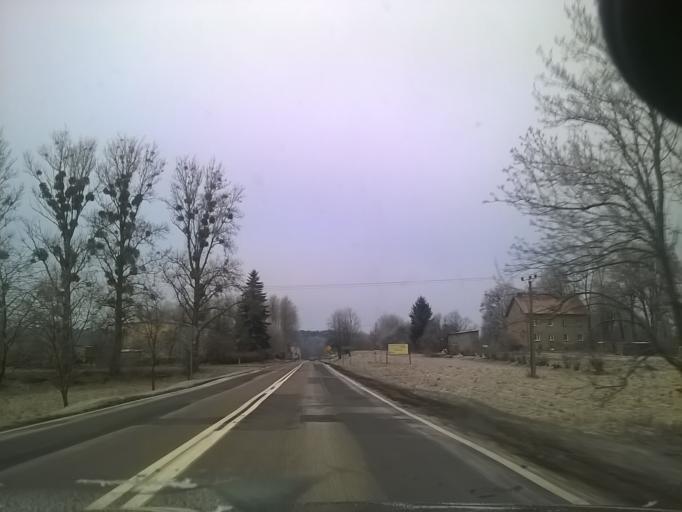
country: PL
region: Warmian-Masurian Voivodeship
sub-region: Powiat mragowski
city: Mragowo
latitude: 53.8439
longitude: 21.1515
